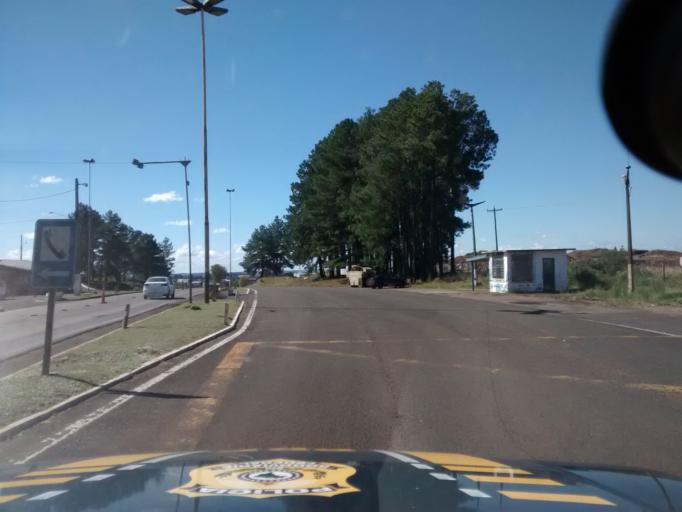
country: BR
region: Rio Grande do Sul
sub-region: Vacaria
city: Vacaria
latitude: -28.4931
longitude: -50.9114
